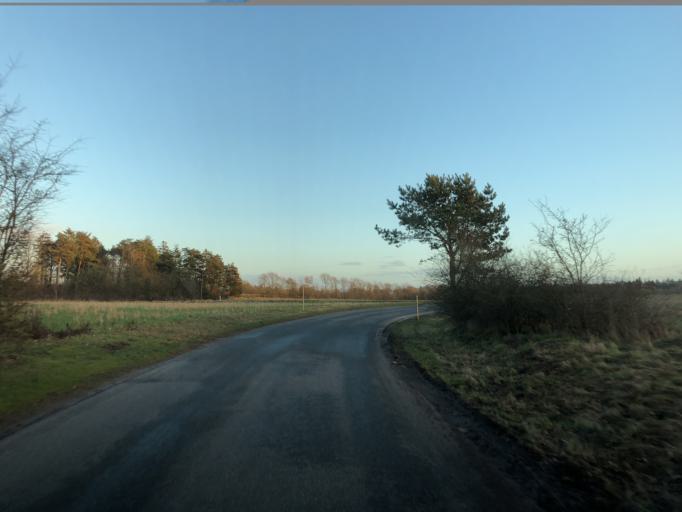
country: DK
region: Central Jutland
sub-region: Skive Kommune
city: Skive
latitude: 56.5426
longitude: 8.9301
